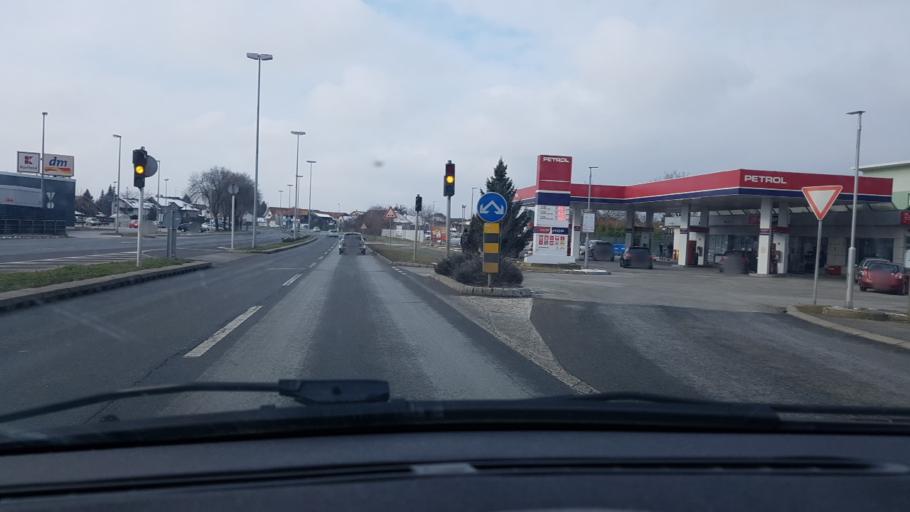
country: HR
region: Varazdinska
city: Varazdin
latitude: 46.3158
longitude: 16.3390
